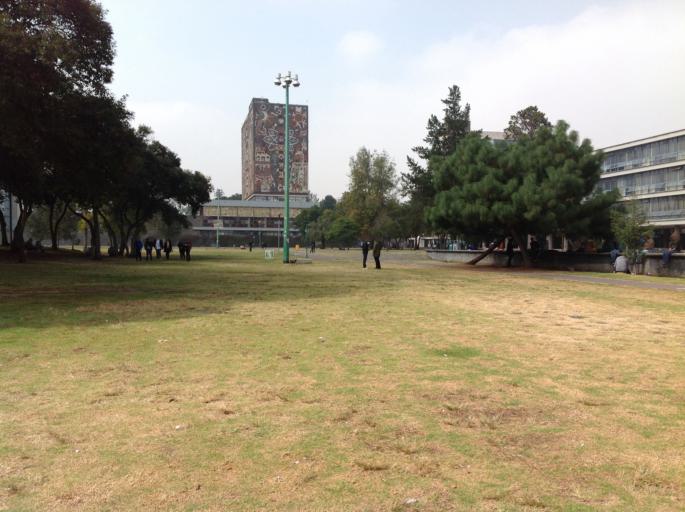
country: MX
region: Mexico City
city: Magdalena Contreras
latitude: 19.3334
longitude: -99.1853
